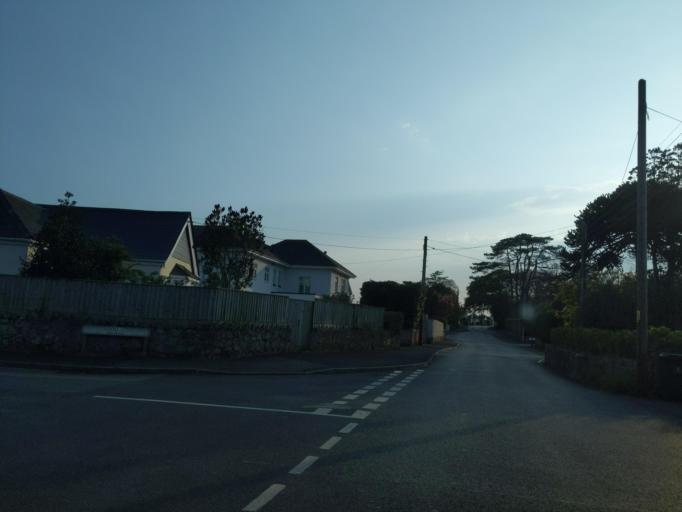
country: GB
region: England
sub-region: Devon
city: Plympton
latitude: 50.3617
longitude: -4.0546
